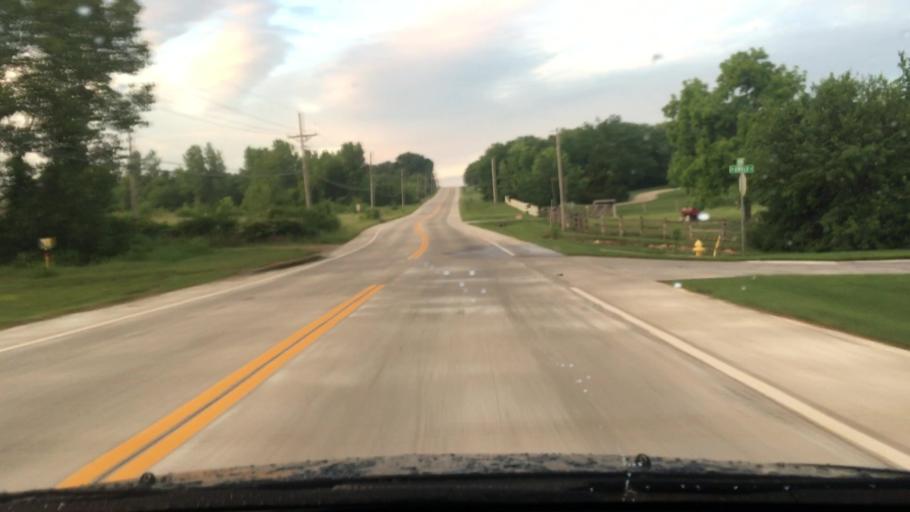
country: US
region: Missouri
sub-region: Jackson County
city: Lees Summit
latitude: 38.8614
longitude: -94.4168
